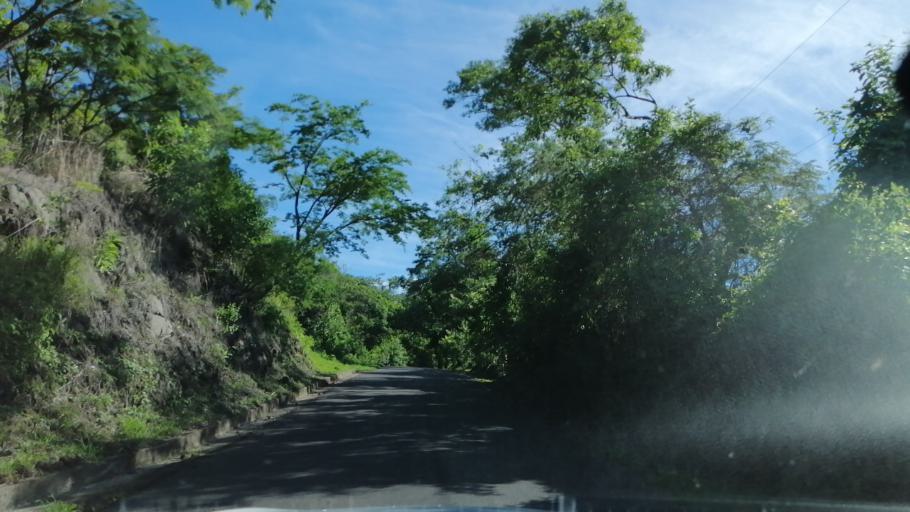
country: SV
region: Morazan
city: Corinto
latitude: 13.8063
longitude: -88.0033
